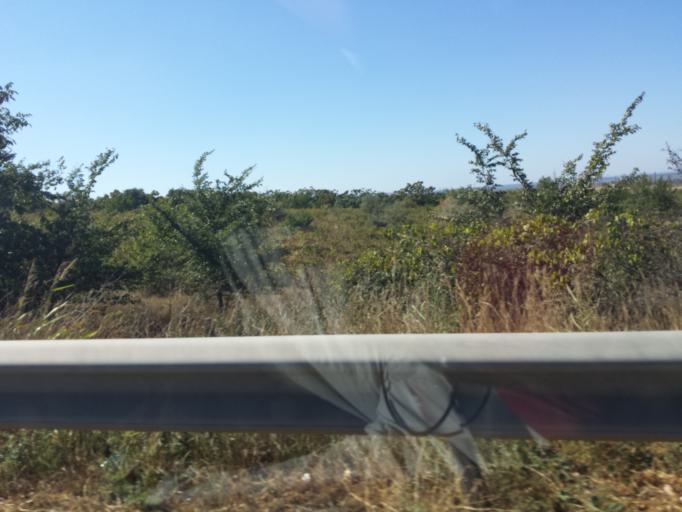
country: RO
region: Tulcea
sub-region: Municipiul Tulcea
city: Tulcea
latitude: 45.1406
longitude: 28.7721
